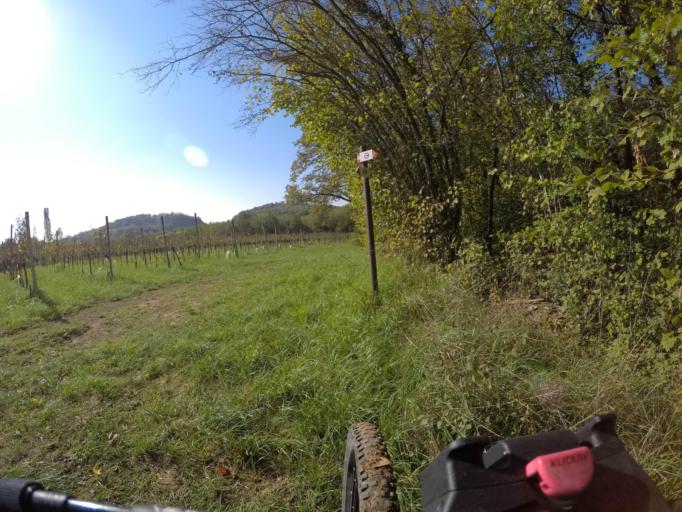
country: IT
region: Friuli Venezia Giulia
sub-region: Provincia di Udine
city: Manzano
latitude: 46.0068
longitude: 13.3743
